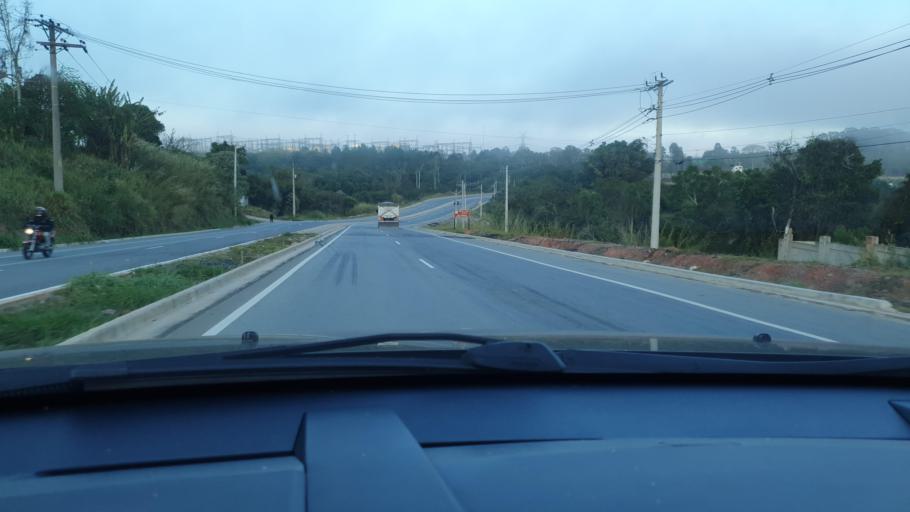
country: BR
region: Sao Paulo
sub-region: Vargem Grande Paulista
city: Vargem Grande Paulista
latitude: -23.6560
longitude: -47.0984
